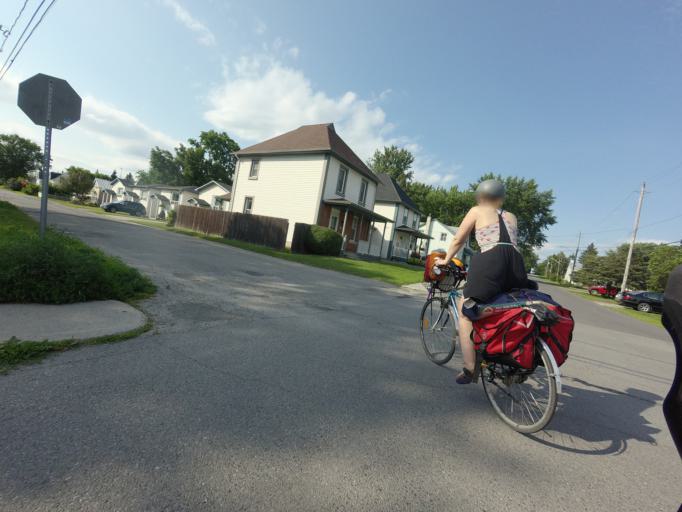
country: CA
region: Ontario
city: Prescott
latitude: 45.0188
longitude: -75.6468
